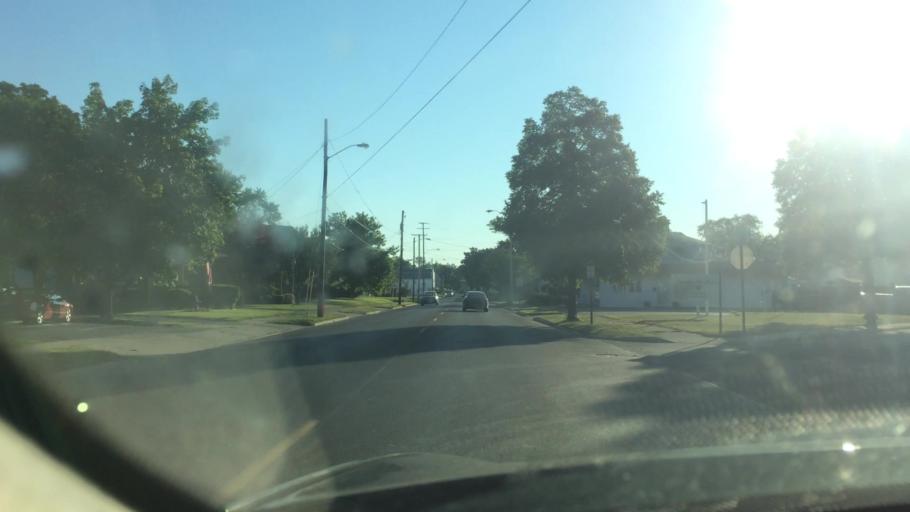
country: US
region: Ohio
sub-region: Hancock County
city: Findlay
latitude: 41.0297
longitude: -83.6565
